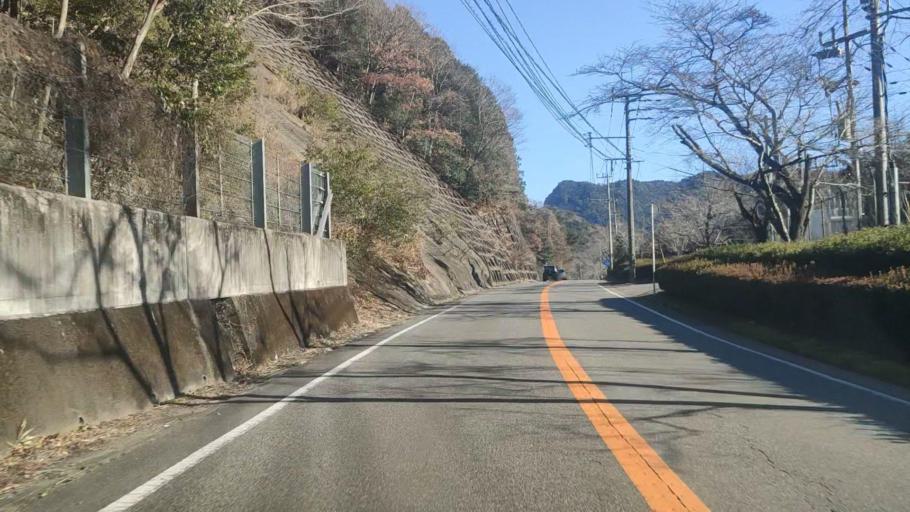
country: JP
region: Miyazaki
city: Nobeoka
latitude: 32.6208
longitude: 131.7062
